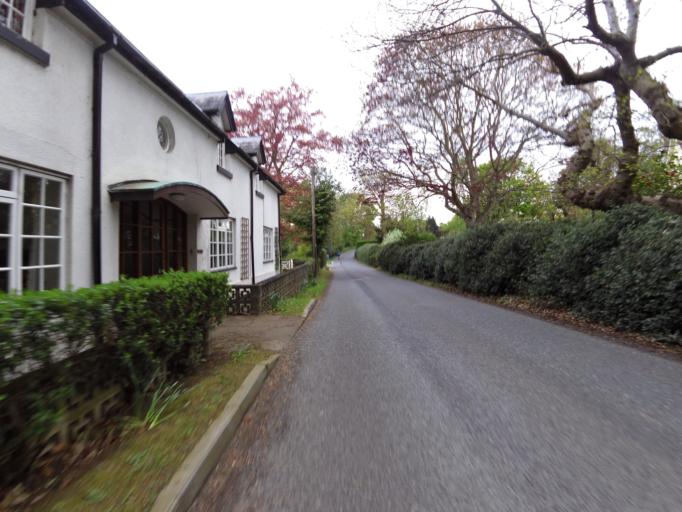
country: GB
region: England
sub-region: Suffolk
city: Kesgrave
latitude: 52.0116
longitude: 1.2340
